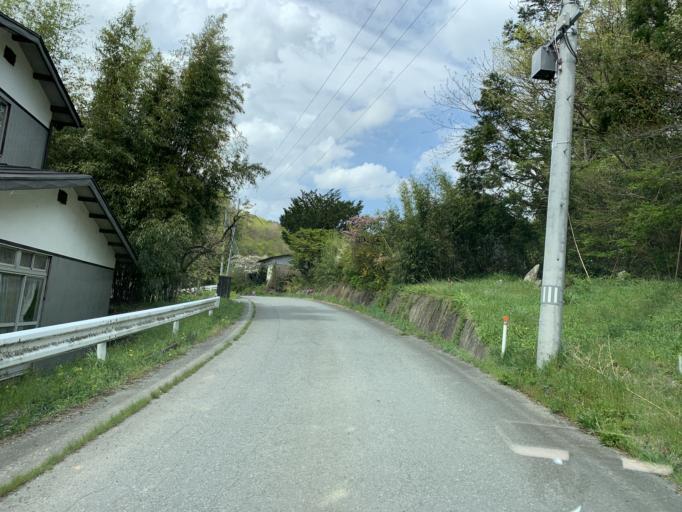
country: JP
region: Iwate
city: Ichinoseki
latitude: 38.7868
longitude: 141.4237
